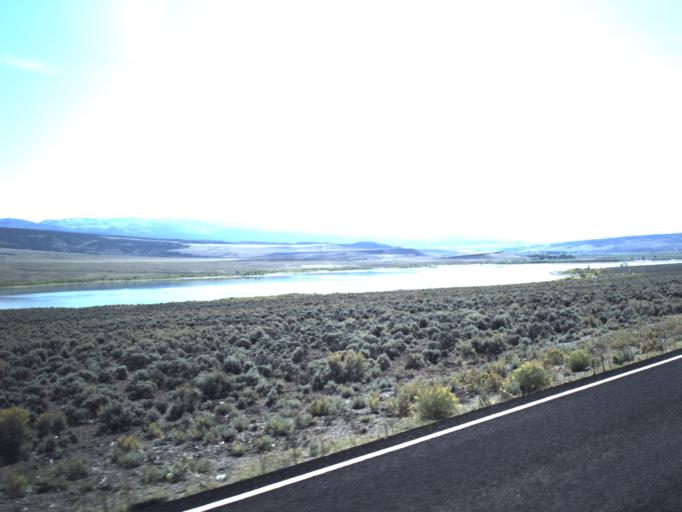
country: US
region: Utah
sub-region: Piute County
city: Junction
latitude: 38.1951
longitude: -112.0105
